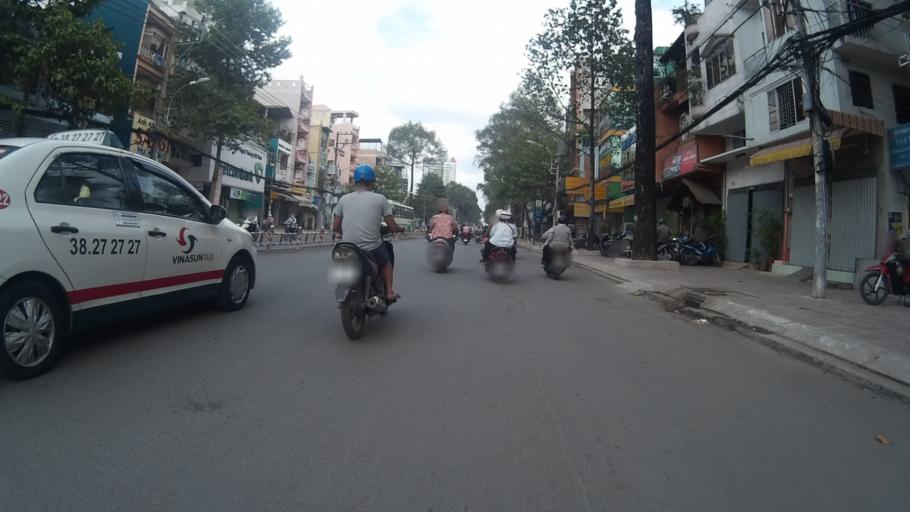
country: VN
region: Ho Chi Minh City
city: Quan Muoi Mot
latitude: 10.7591
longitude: 106.6516
